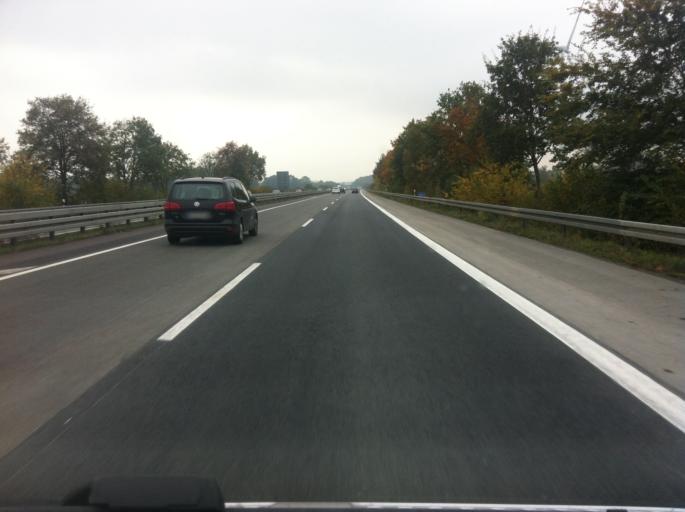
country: DE
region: North Rhine-Westphalia
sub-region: Regierungsbezirk Munster
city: Gescher
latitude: 51.9317
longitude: 7.0394
